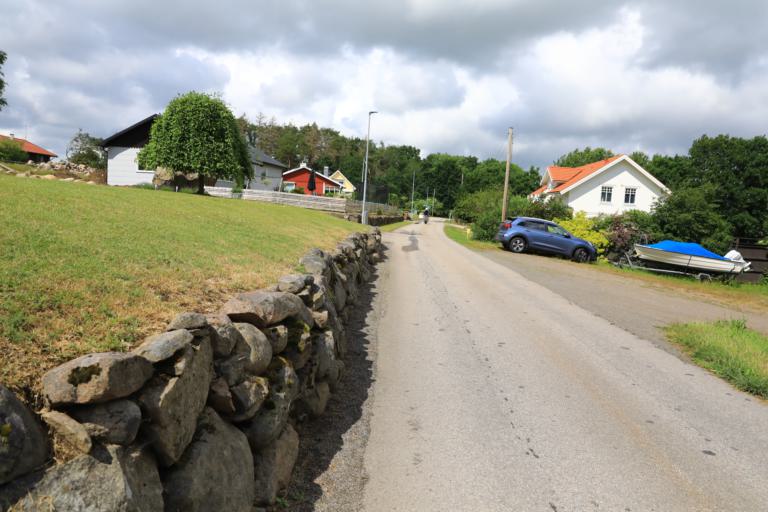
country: SE
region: Halland
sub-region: Varbergs Kommun
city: Varberg
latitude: 57.1776
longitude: 12.2979
